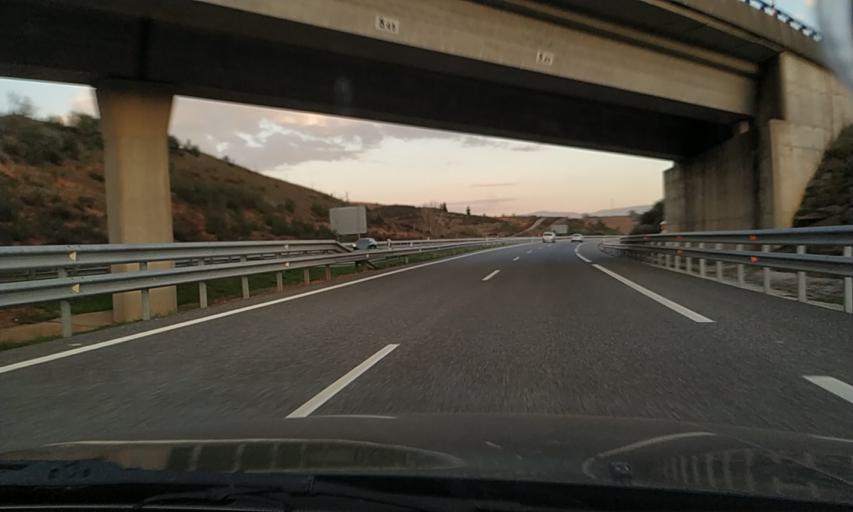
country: ES
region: Castille and Leon
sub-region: Provincia de Leon
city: Villadecanes
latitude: 42.5843
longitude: -6.7876
